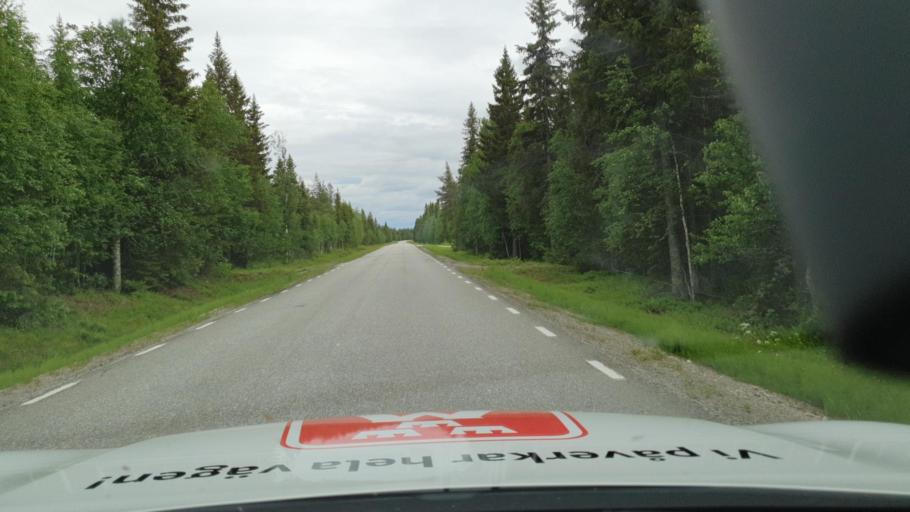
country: SE
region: Vaesterbotten
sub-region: Lycksele Kommun
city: Soderfors
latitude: 64.3503
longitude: 18.1298
